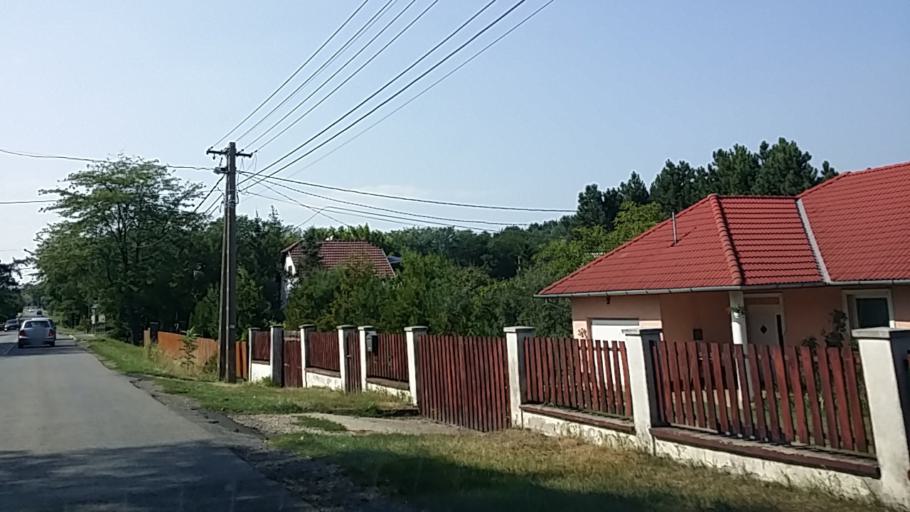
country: HU
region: Pest
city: Erdokertes
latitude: 47.6715
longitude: 19.3247
